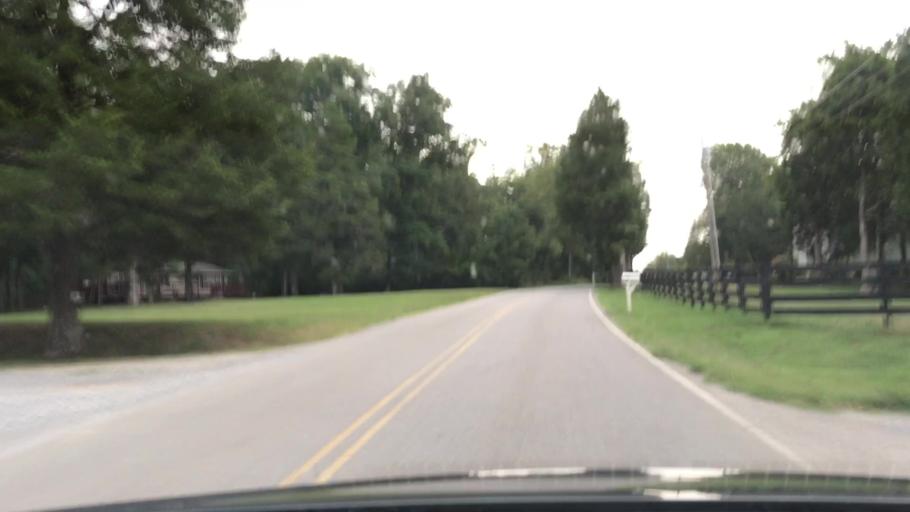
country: US
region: Tennessee
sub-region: Williamson County
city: Nolensville
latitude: 35.9765
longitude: -86.6645
